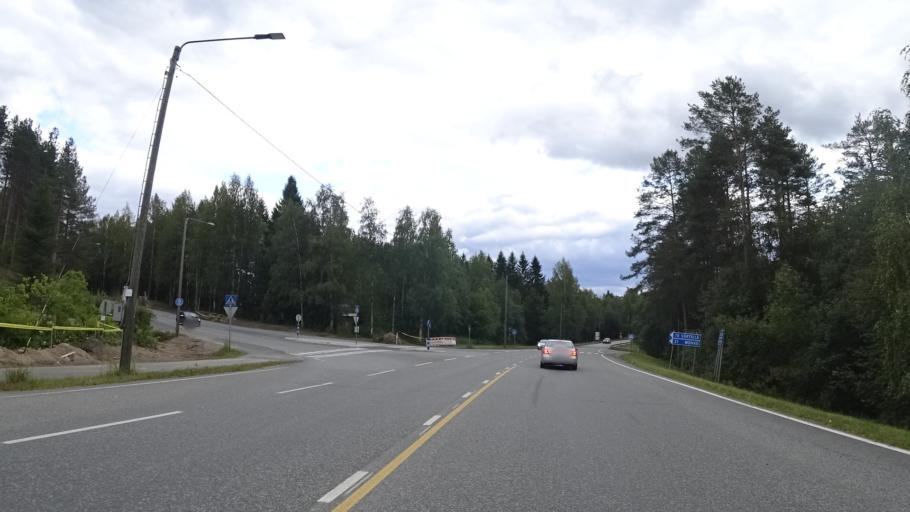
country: FI
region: North Karelia
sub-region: Joensuu
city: Ilomantsi
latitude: 62.6548
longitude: 30.9353
